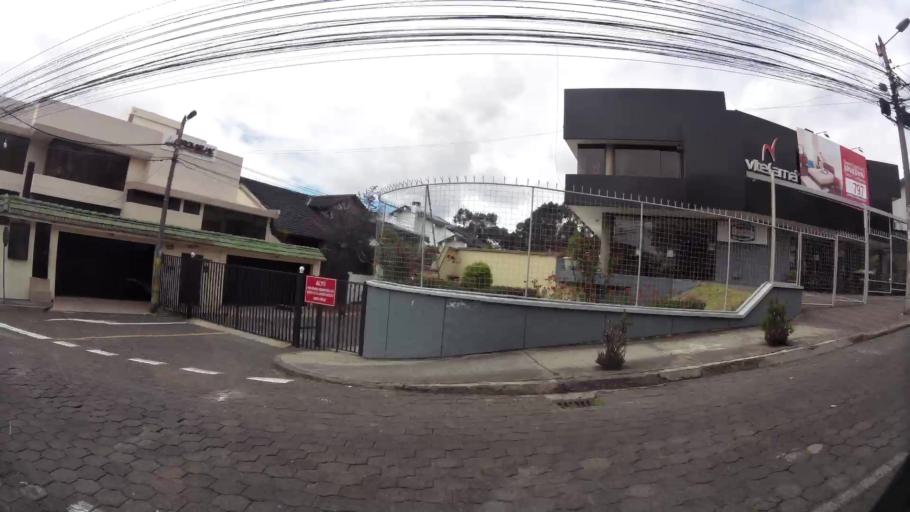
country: EC
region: Pichincha
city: Quito
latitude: -0.1603
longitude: -78.4927
